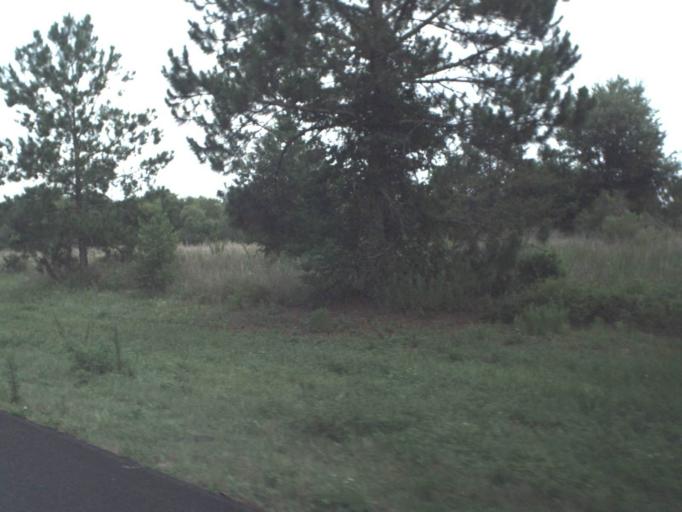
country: US
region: Florida
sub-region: Baker County
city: Macclenny
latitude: 30.1492
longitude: -82.0338
